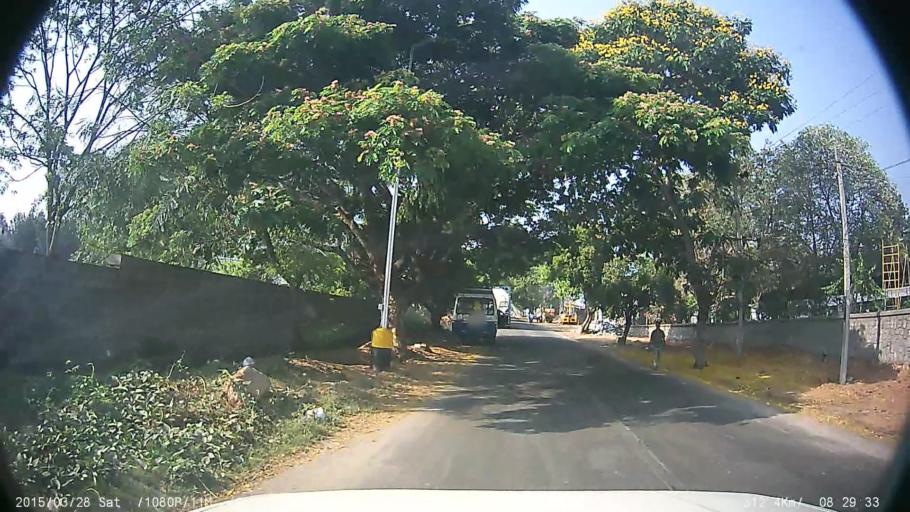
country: IN
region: Karnataka
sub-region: Mysore
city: Mysore
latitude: 12.3642
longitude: 76.6062
